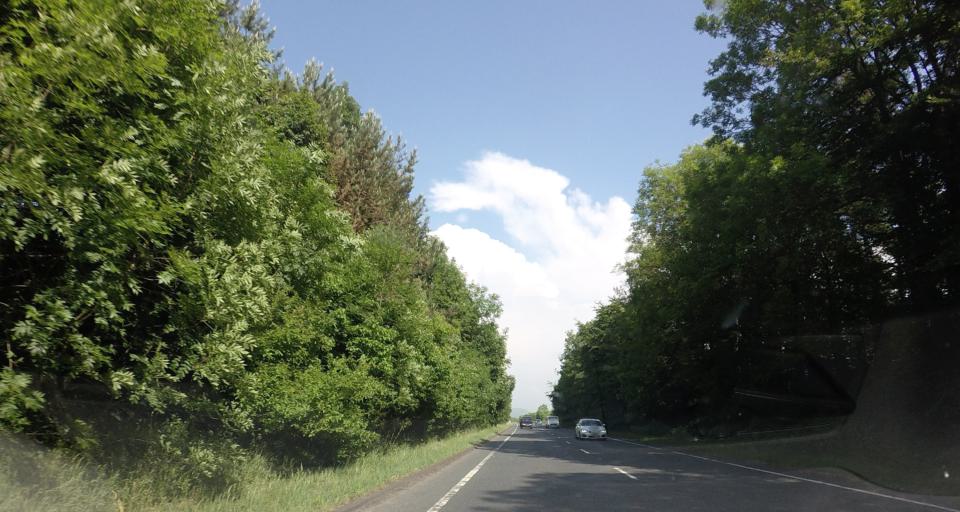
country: GB
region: England
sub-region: Cumbria
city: Cockermouth
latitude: 54.6507
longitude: -3.3576
